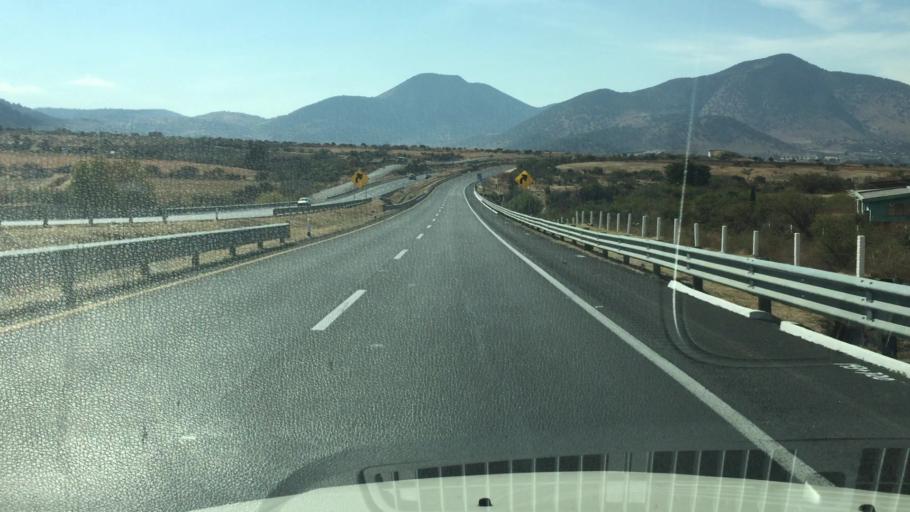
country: MX
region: Michoacan
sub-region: Contepec
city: La Higuerilla (Los Lirios)
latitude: 19.8829
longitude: -100.2750
